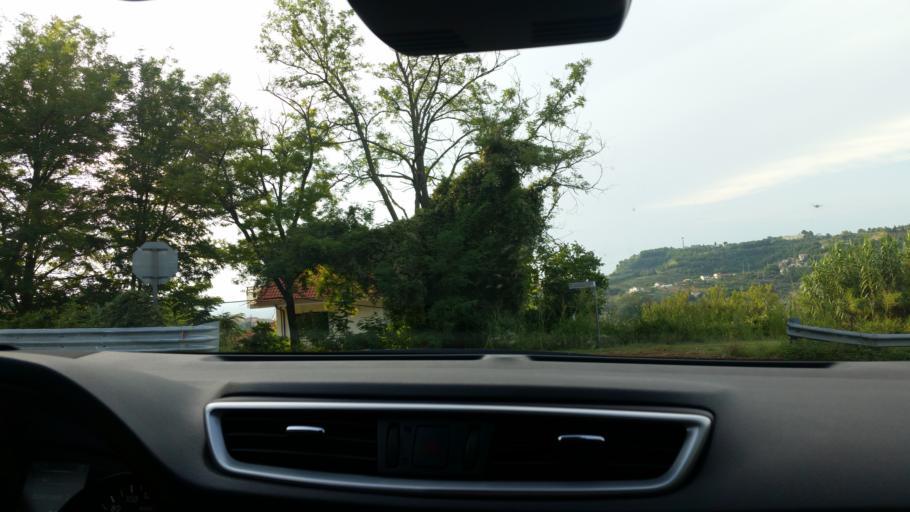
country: IT
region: Abruzzo
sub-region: Provincia di Chieti
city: Torrevecchia
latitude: 42.3537
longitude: 14.1829
